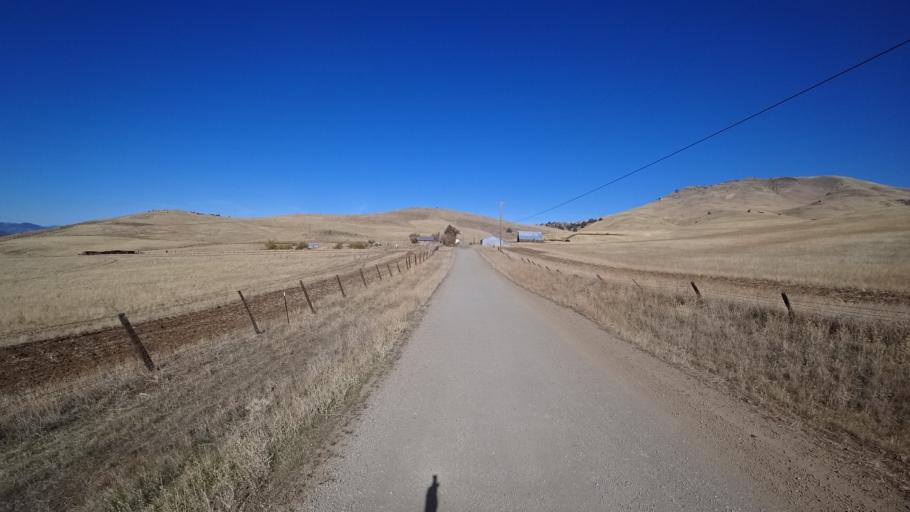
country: US
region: California
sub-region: Siskiyou County
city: Montague
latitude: 41.8420
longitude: -122.4206
